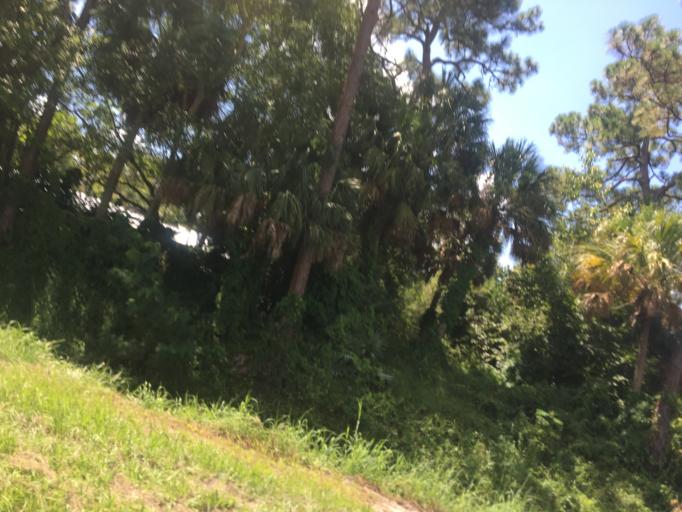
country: US
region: Florida
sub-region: Martin County
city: Palm City
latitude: 27.1592
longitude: -80.2922
